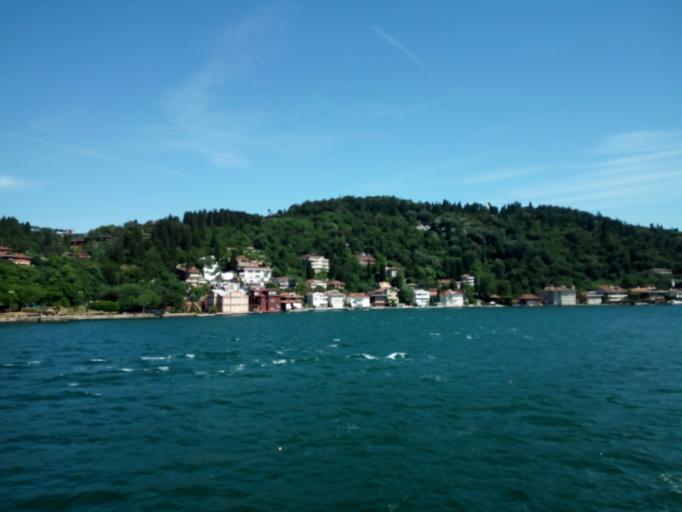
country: TR
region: Istanbul
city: UEskuedar
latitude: 41.0689
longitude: 29.0541
